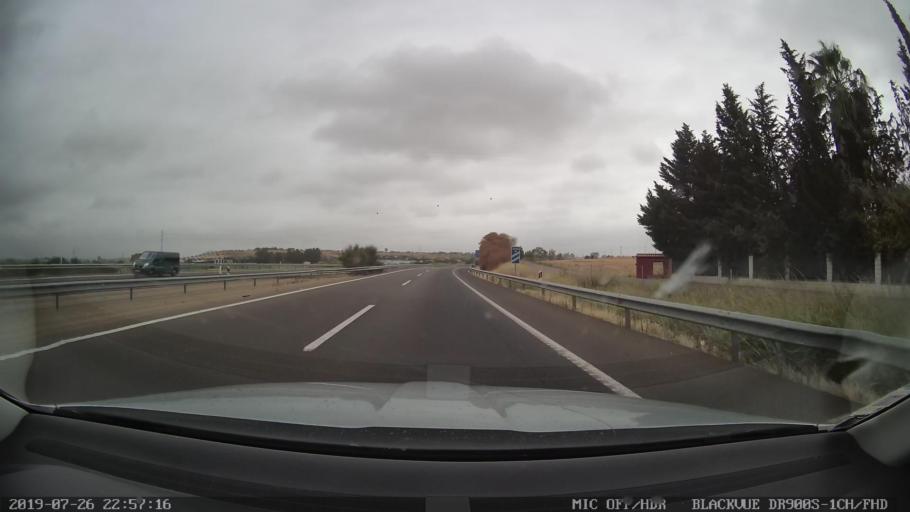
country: ES
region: Extremadura
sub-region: Provincia de Badajoz
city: Calamonte
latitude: 38.9052
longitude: -6.4012
